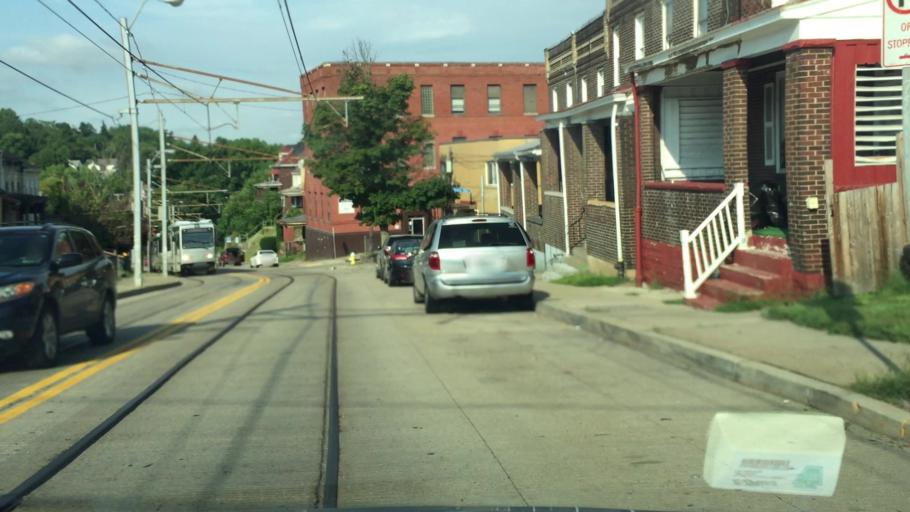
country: US
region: Pennsylvania
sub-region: Allegheny County
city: Mount Oliver
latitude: 40.4217
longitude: -79.9976
